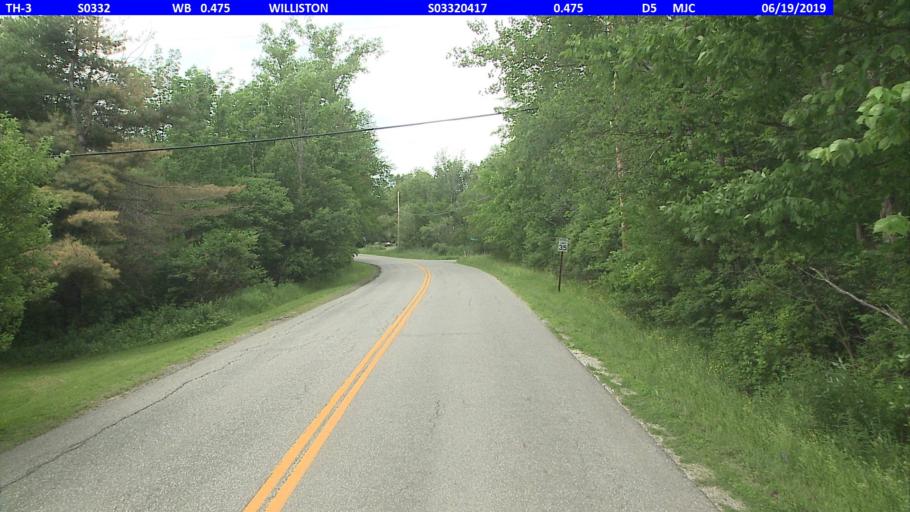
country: US
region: Vermont
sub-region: Chittenden County
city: Williston
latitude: 44.4250
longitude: -73.1130
